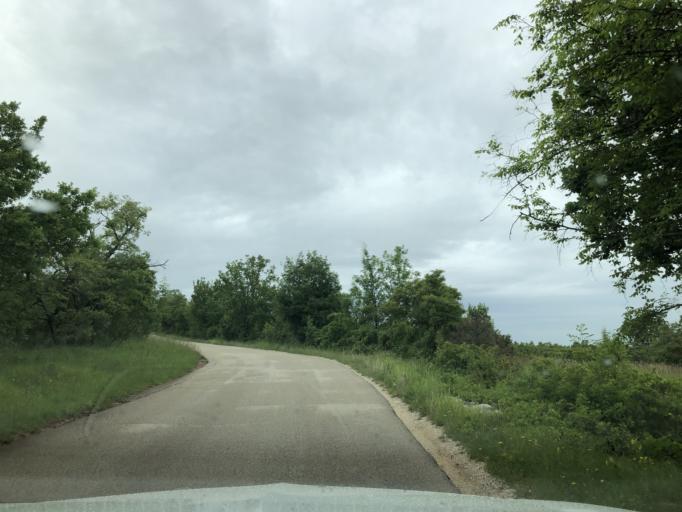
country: HR
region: Istarska
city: Buje
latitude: 45.4358
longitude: 13.6759
